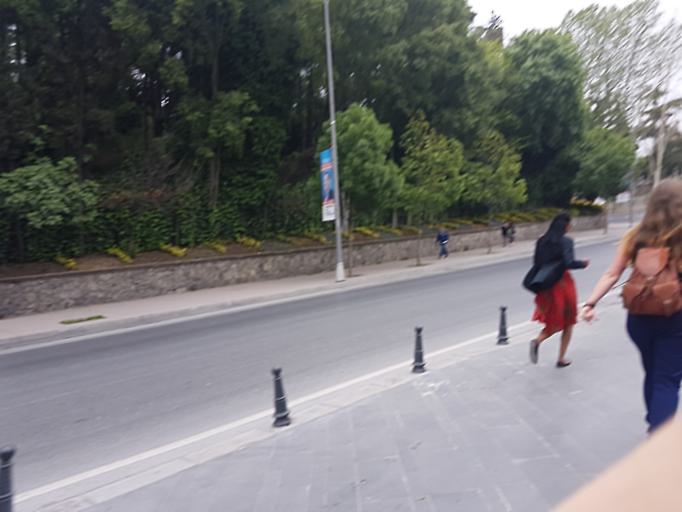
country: TR
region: Istanbul
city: Sisli
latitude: 41.0392
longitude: 28.9958
